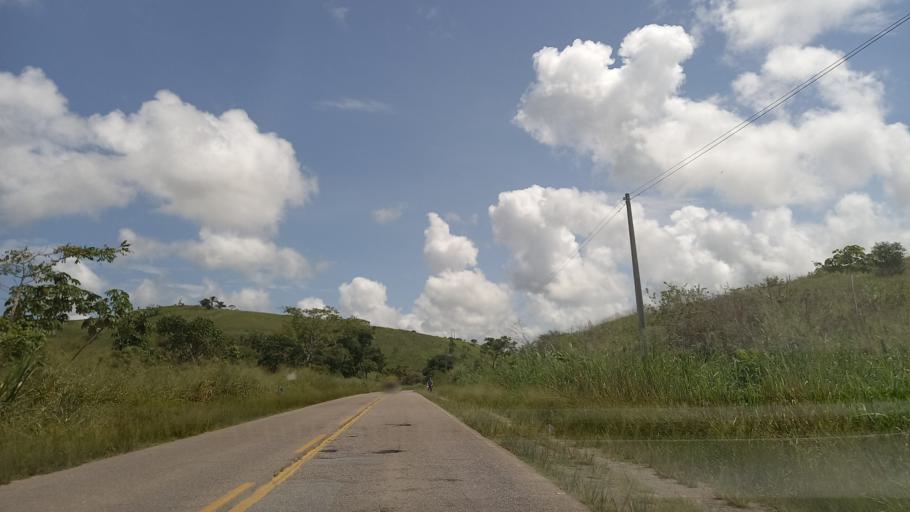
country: BR
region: Pernambuco
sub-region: Barreiros
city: Barreiros
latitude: -8.7829
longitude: -35.1781
